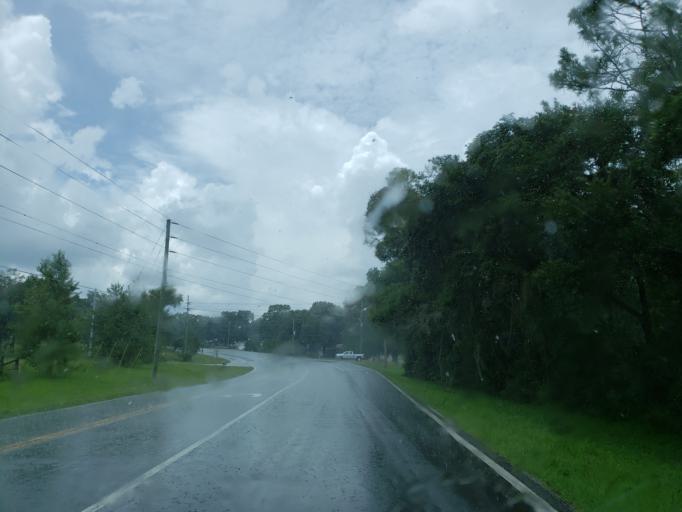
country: US
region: Florida
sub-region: Citrus County
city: Floral City
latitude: 28.6451
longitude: -82.3006
